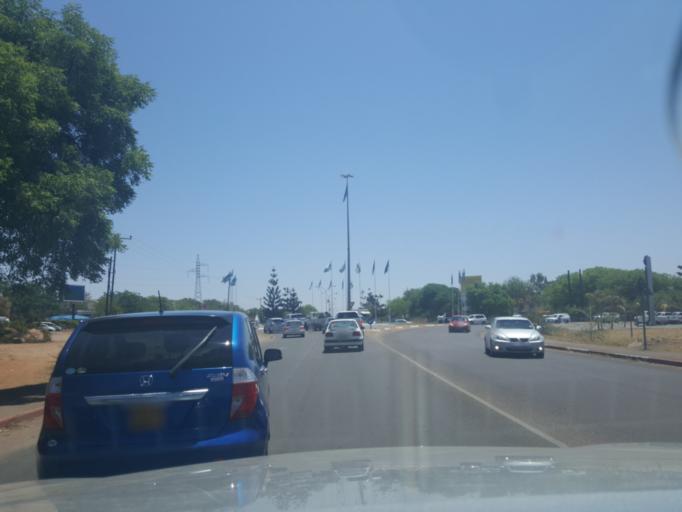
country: BW
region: South East
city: Gaborone
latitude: -24.6878
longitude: 25.8844
